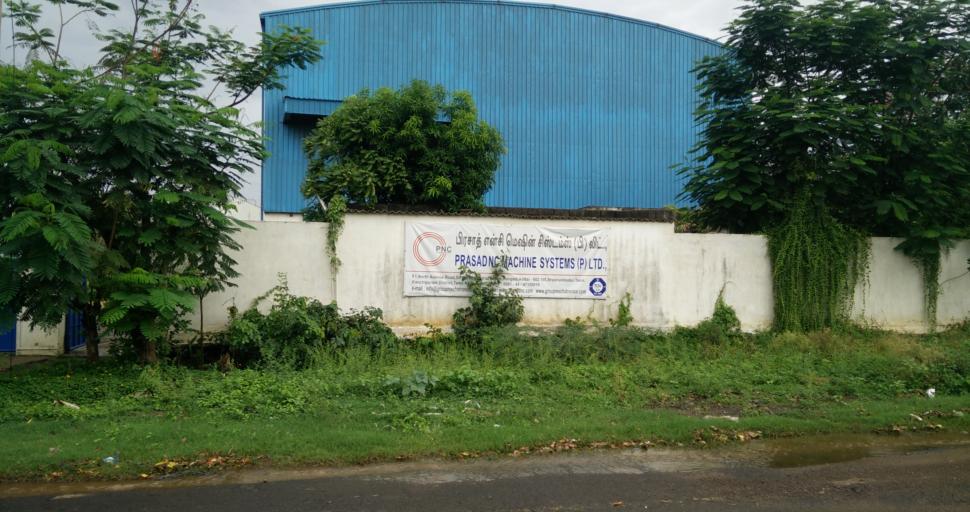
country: IN
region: Tamil Nadu
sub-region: Kancheepuram
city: Nandambakkam
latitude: 12.9996
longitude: 80.0258
